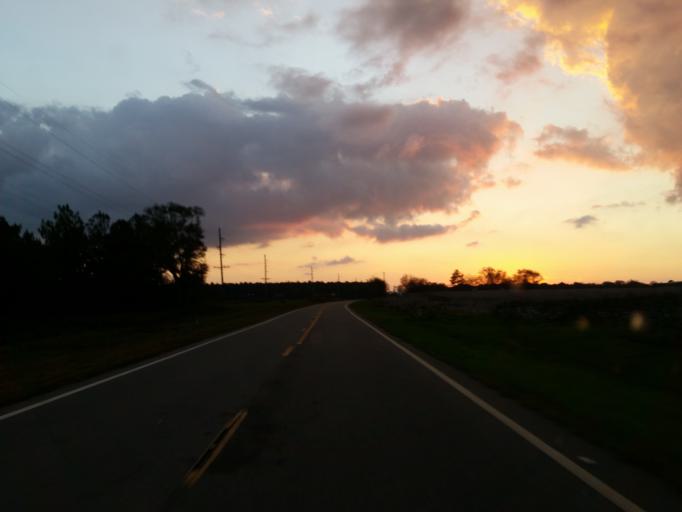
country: US
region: Georgia
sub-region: Dooly County
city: Vienna
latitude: 32.1382
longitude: -83.6839
